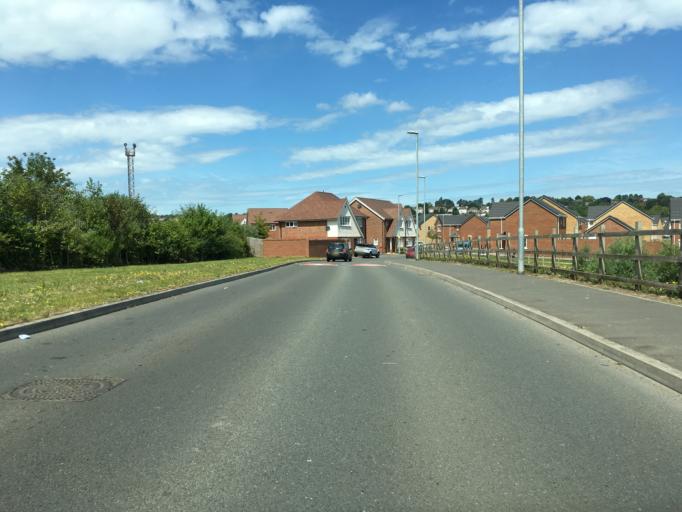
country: GB
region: Wales
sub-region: Newport
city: Newport
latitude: 51.5724
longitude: -2.9986
